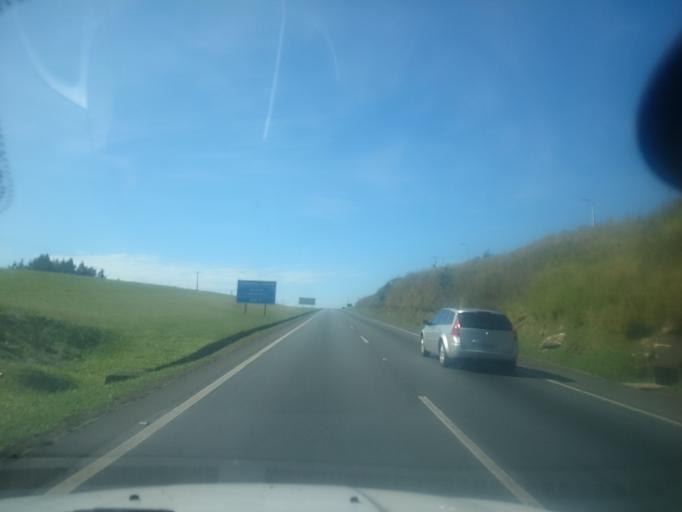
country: BR
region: Parana
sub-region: Campo Largo
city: Campo Largo
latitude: -25.4755
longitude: -49.7091
